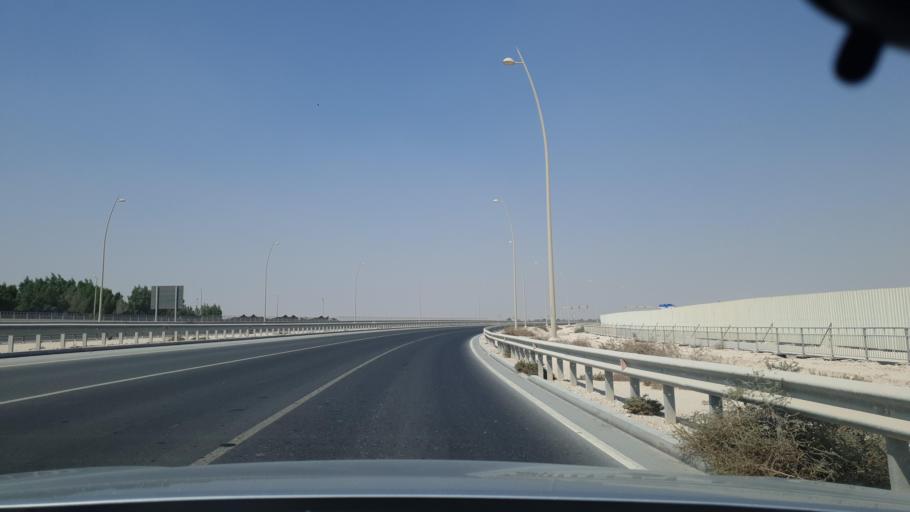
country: QA
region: Al Khawr
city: Al Khawr
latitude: 25.6610
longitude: 51.4809
